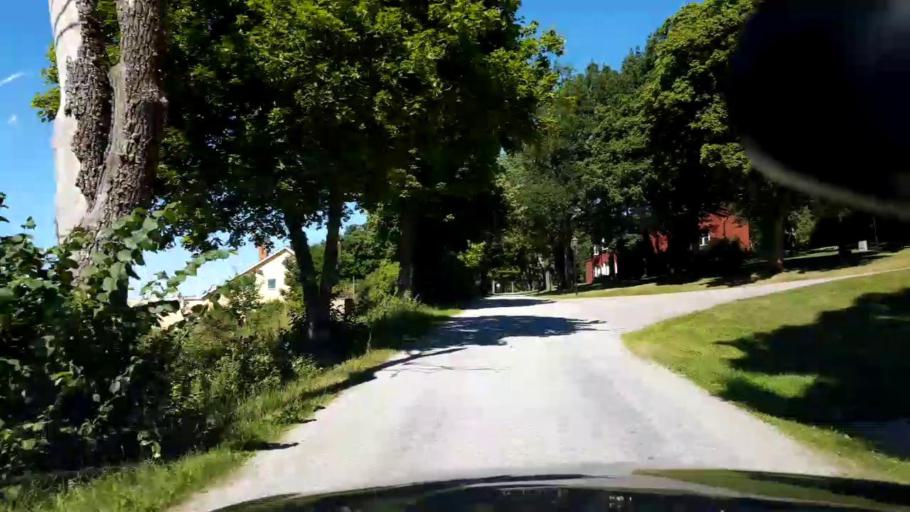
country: SE
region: Stockholm
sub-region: Sigtuna Kommun
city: Sigtuna
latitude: 59.6077
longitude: 17.6422
